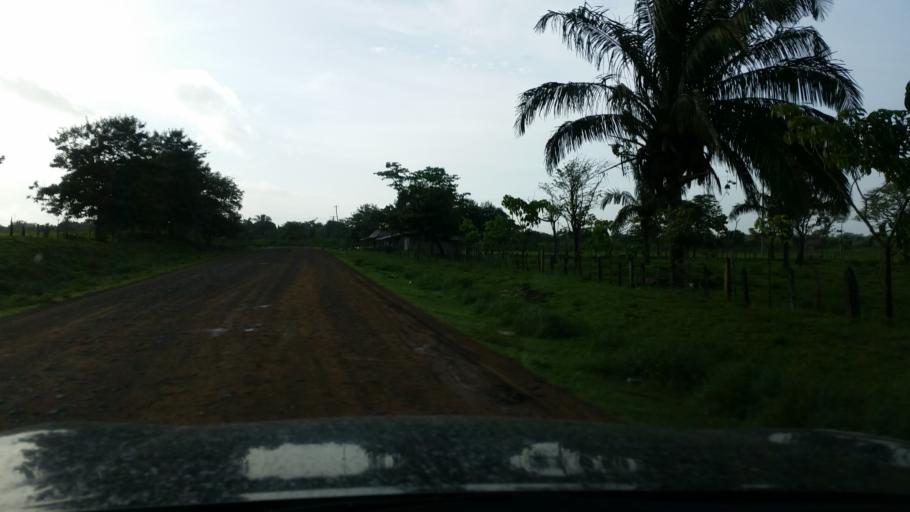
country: NI
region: Atlantico Norte (RAAN)
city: Bonanza
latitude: 14.0650
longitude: -84.0014
